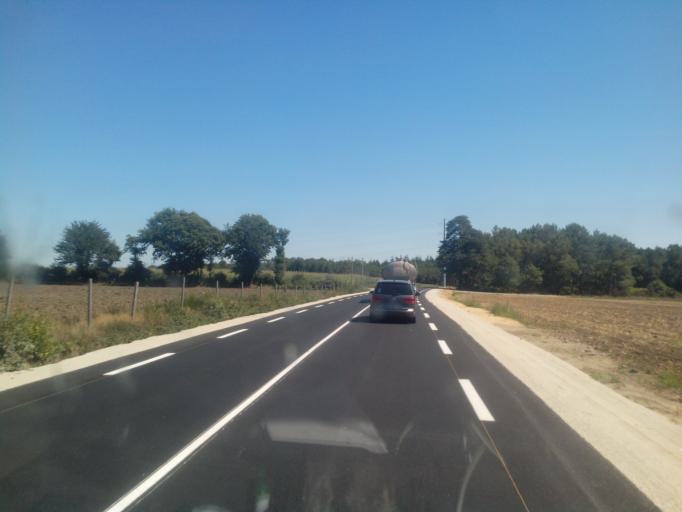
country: FR
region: Brittany
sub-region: Departement du Morbihan
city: Guillac
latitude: 47.8729
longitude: -2.4867
